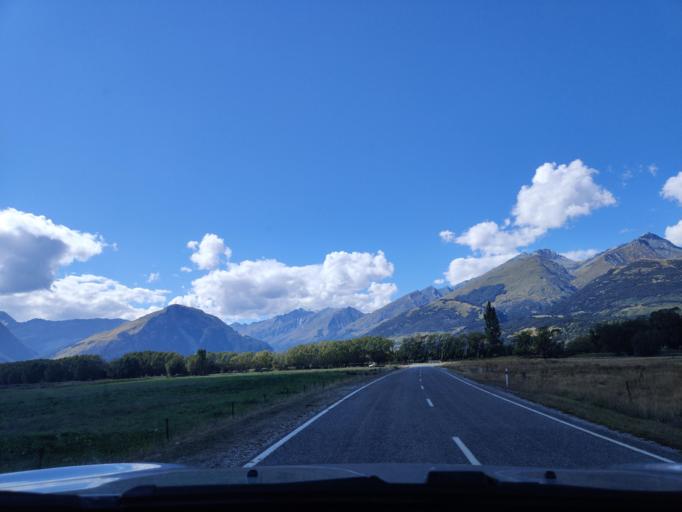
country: NZ
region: Otago
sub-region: Queenstown-Lakes District
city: Queenstown
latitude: -44.7839
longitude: 168.3925
